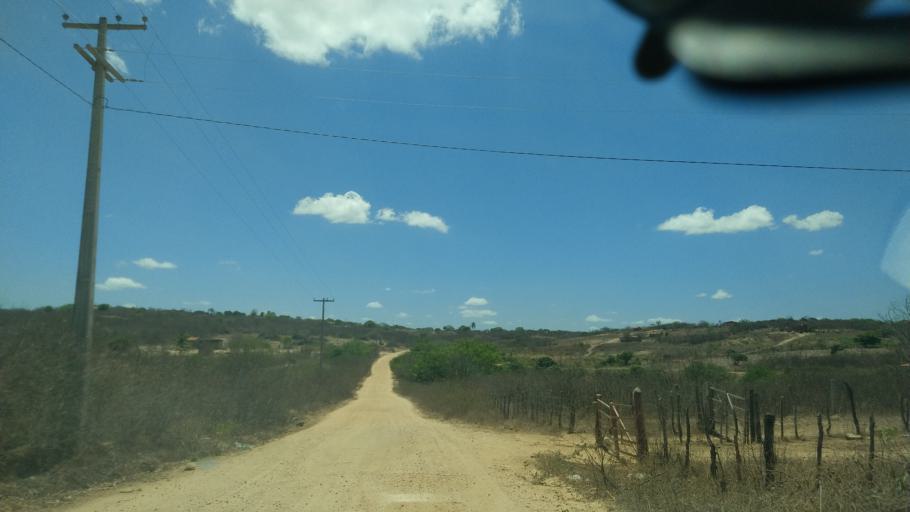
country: BR
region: Rio Grande do Norte
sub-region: Cerro Cora
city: Cerro Cora
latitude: -6.0192
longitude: -36.3313
